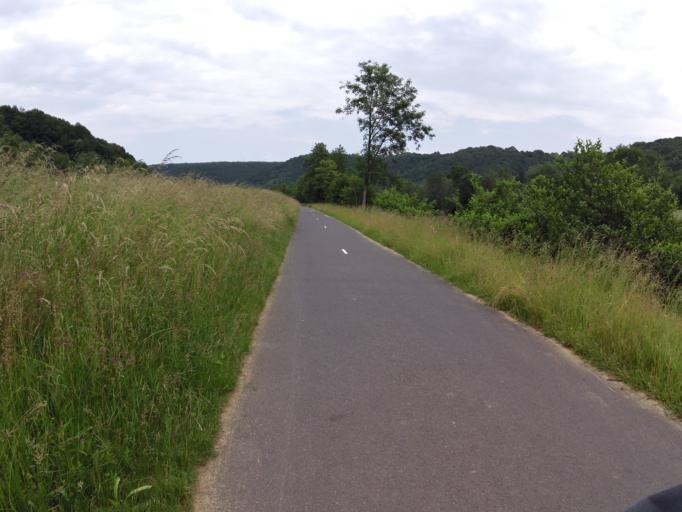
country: FR
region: Champagne-Ardenne
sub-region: Departement des Ardennes
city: Aiglemont
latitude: 49.7871
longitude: 4.7554
